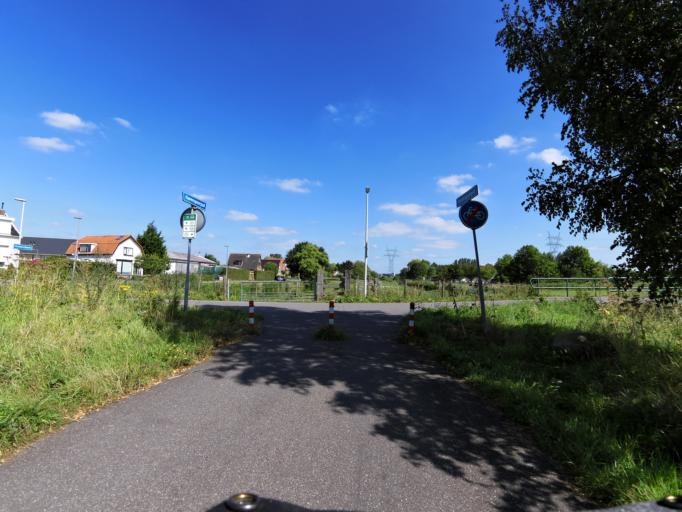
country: NL
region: South Holland
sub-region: Gemeente Barendrecht
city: Barendrecht
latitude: 51.8688
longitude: 4.5290
